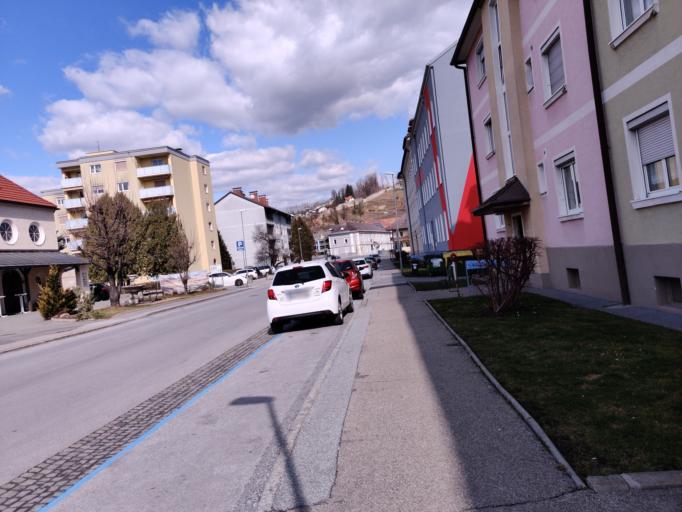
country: AT
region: Styria
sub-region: Politischer Bezirk Voitsberg
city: Voitsberg
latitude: 47.0465
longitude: 15.1484
